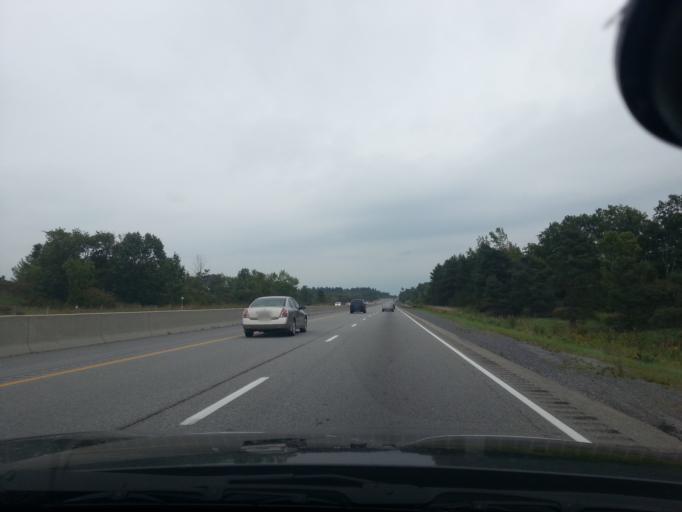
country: CA
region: Ontario
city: Gananoque
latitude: 44.3246
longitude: -76.3109
